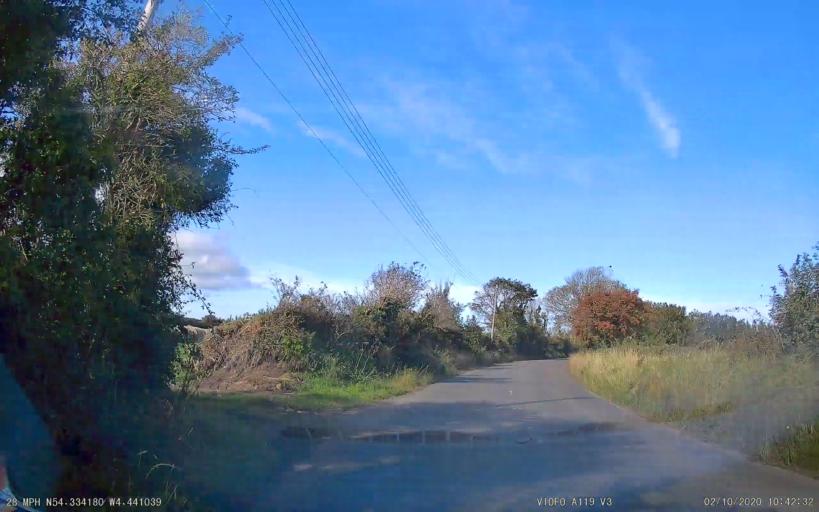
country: IM
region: Ramsey
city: Ramsey
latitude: 54.3342
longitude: -4.4410
